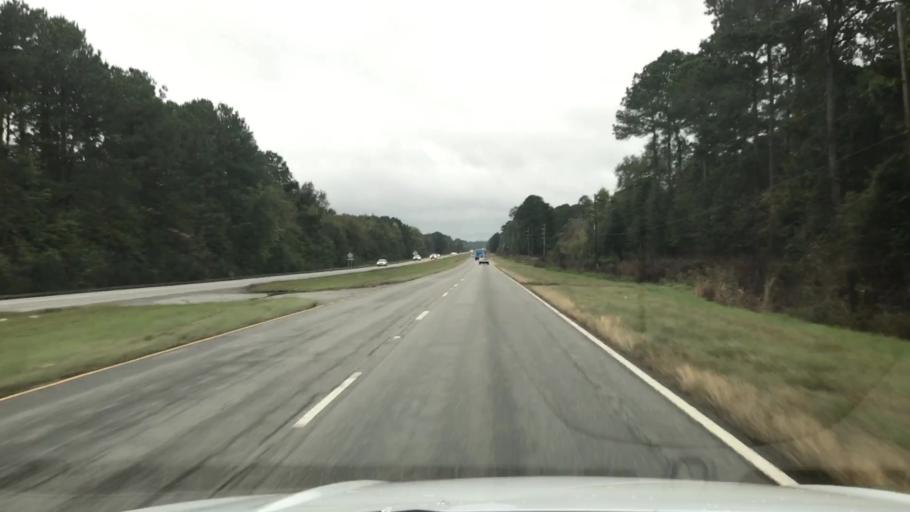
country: US
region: South Carolina
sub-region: Charleston County
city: Ravenel
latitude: 32.7600
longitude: -80.3992
